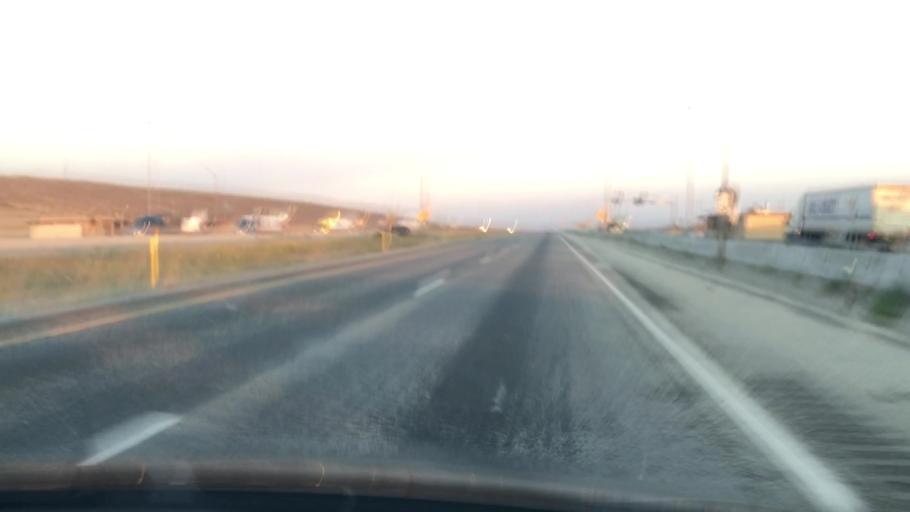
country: US
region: Idaho
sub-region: Minidoka County
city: Rupert
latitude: 42.5051
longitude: -113.4089
